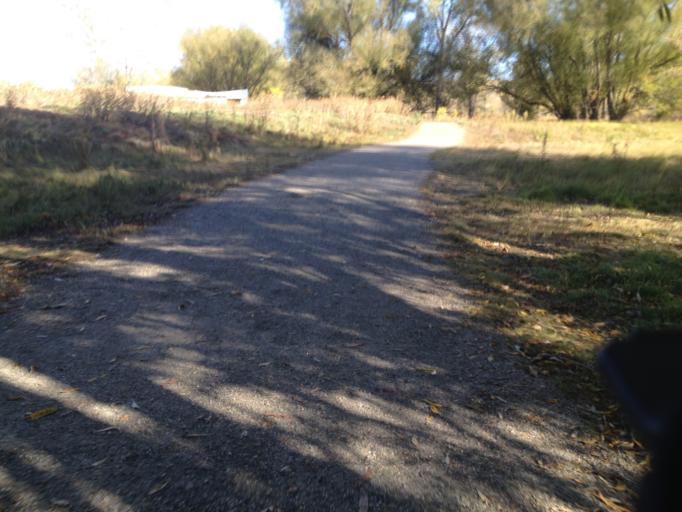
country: US
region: Colorado
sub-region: Boulder County
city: Boulder
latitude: 39.9680
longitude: -105.2327
